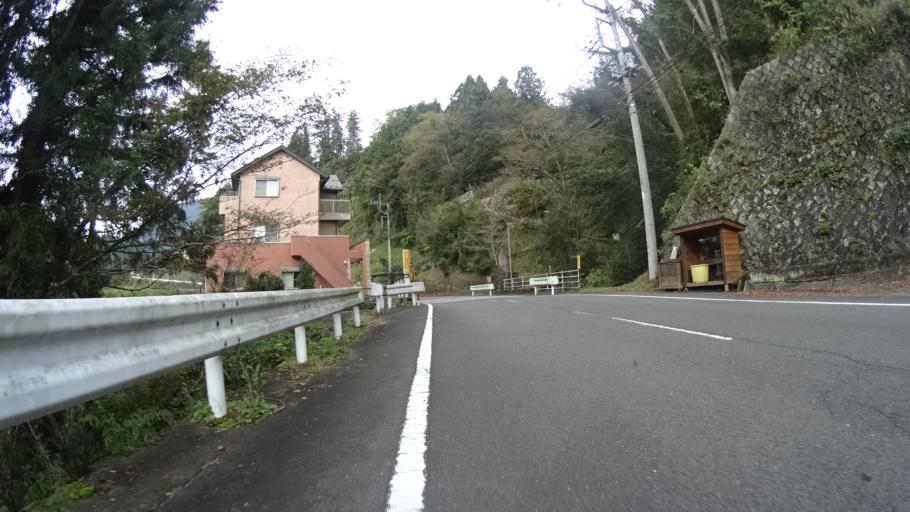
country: JP
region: Yamanashi
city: Uenohara
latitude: 35.6361
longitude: 139.0611
